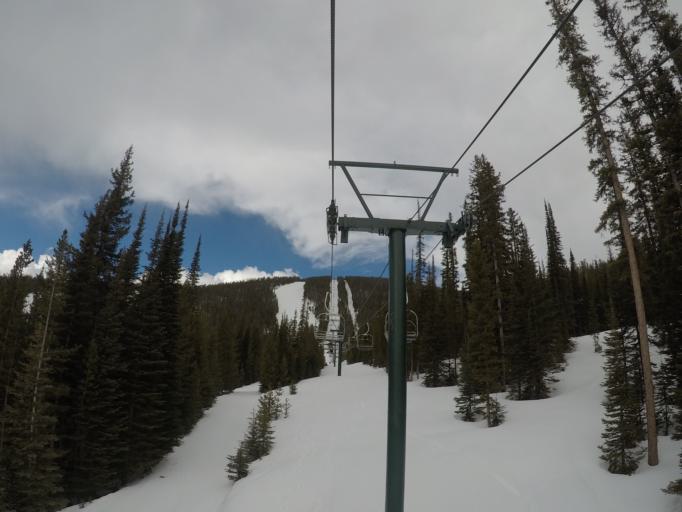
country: US
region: Montana
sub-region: Granite County
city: Philipsburg
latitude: 46.2520
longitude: -113.2415
